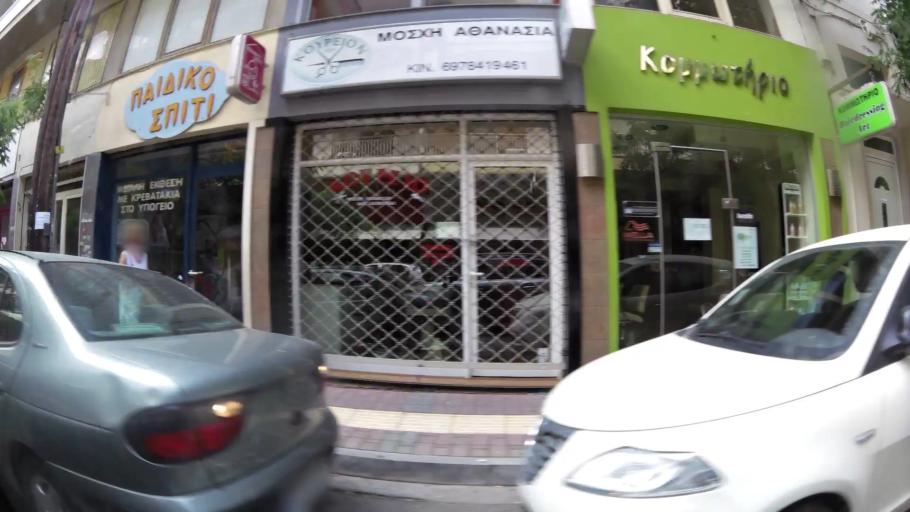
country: GR
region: Central Macedonia
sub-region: Nomos Pierias
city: Katerini
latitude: 40.2735
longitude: 22.5081
